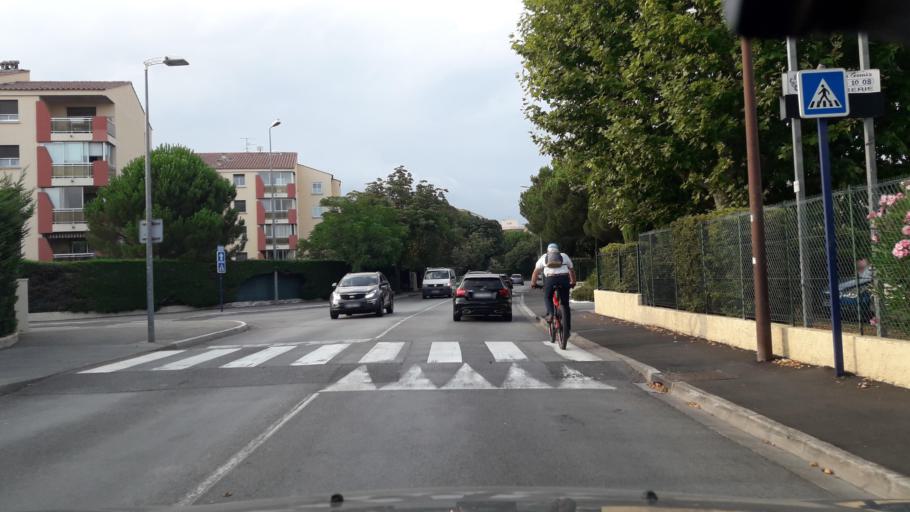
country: FR
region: Provence-Alpes-Cote d'Azur
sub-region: Departement du Var
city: Frejus
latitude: 43.4356
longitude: 6.7540
